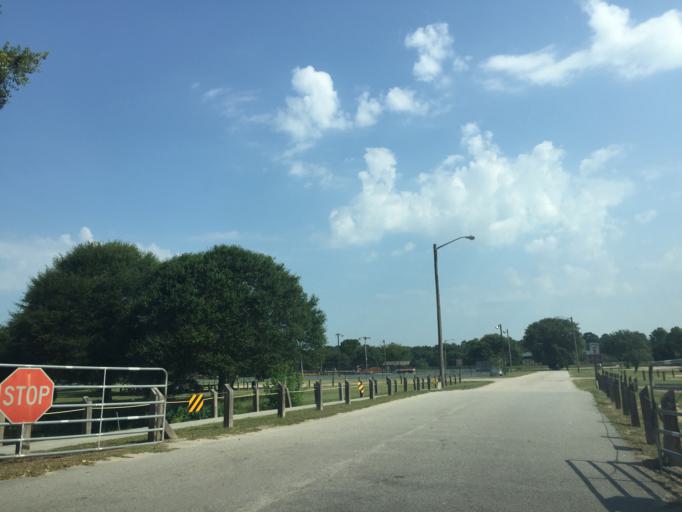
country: US
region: Georgia
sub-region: Chatham County
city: Isle of Hope
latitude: 31.9908
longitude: -81.0878
